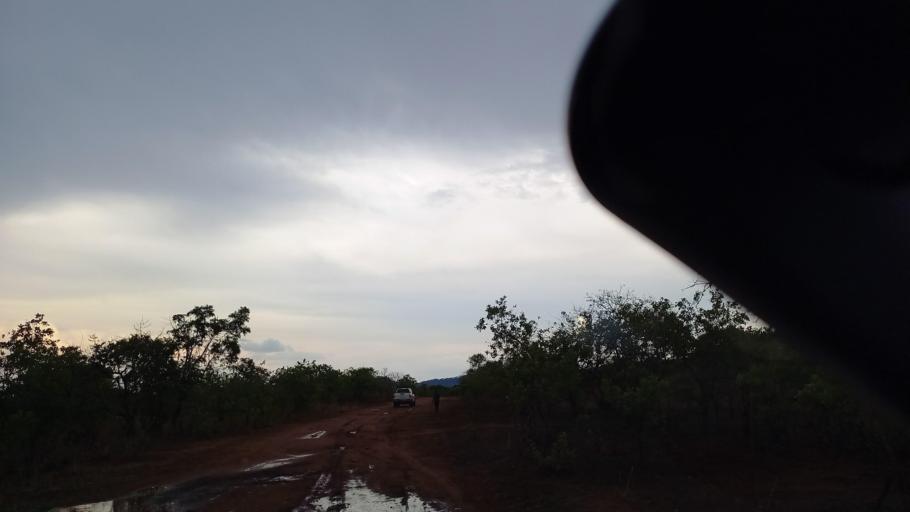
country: ZM
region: Lusaka
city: Kafue
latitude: -16.0254
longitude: 28.2982
